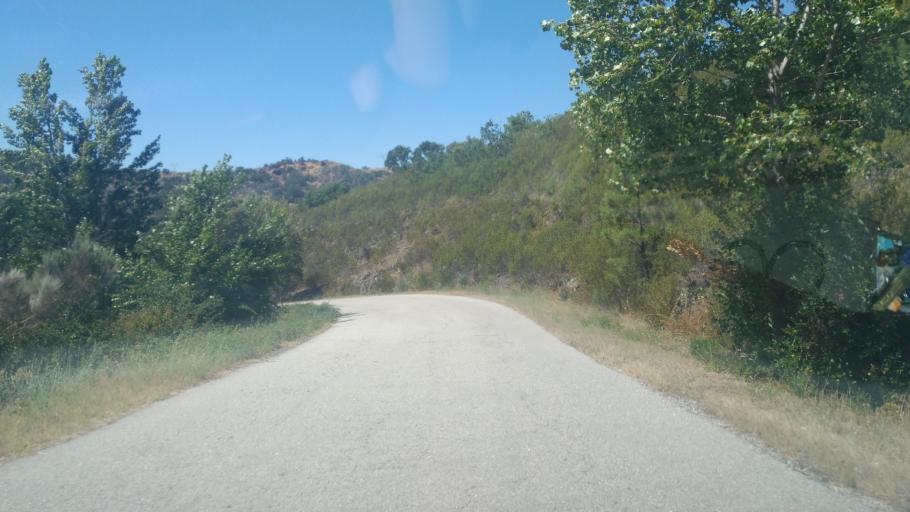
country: ES
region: Castille and Leon
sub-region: Provincia de Salamanca
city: Mieza
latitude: 41.1885
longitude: -6.6540
